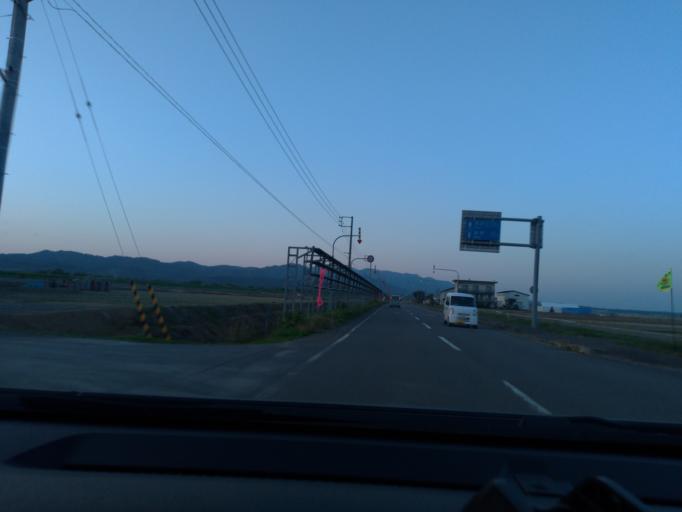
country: JP
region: Hokkaido
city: Iwamizawa
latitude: 43.3309
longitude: 141.7034
